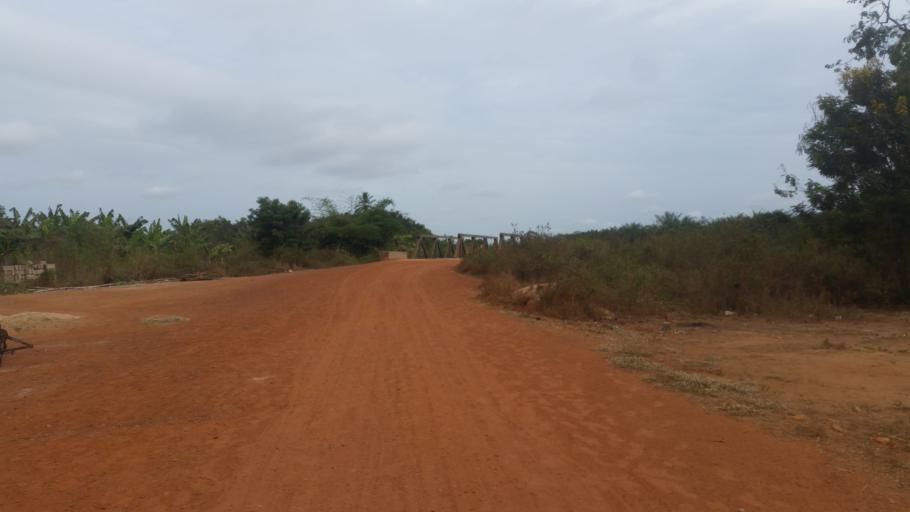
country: GH
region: Central
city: Cape Coast
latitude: 5.1261
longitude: -1.3022
